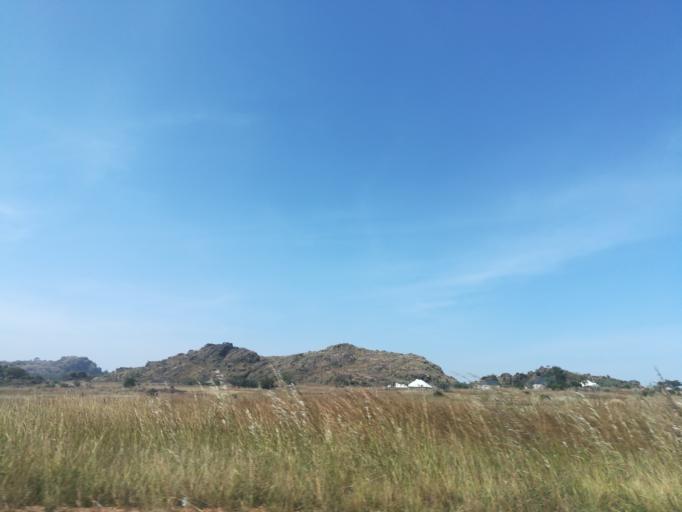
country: NG
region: Plateau
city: Bukuru
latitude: 9.7694
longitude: 8.9012
